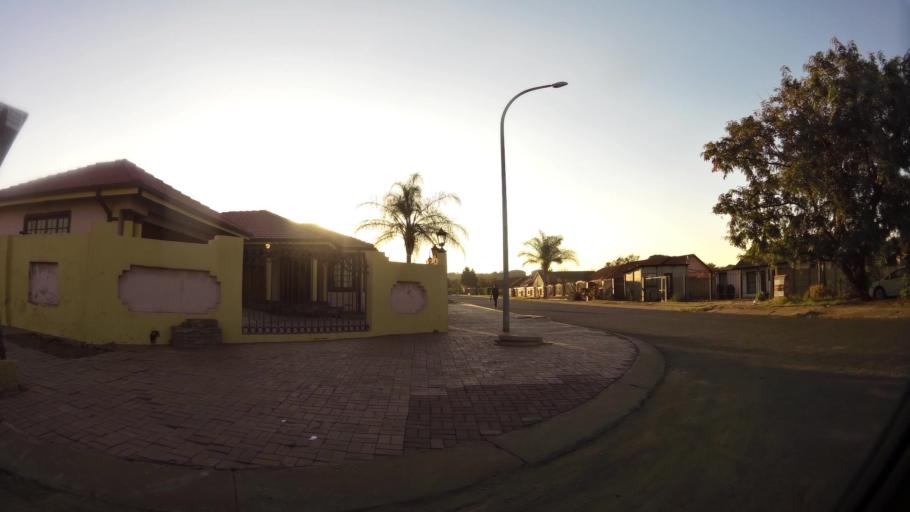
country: ZA
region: North-West
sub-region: Bojanala Platinum District Municipality
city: Rustenburg
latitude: -25.6380
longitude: 27.2046
